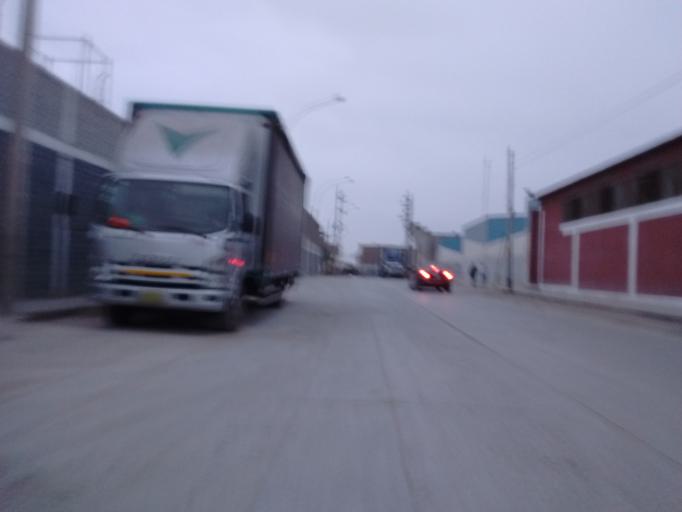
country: PE
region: Callao
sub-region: Callao
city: Callao
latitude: -12.0399
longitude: -77.0802
